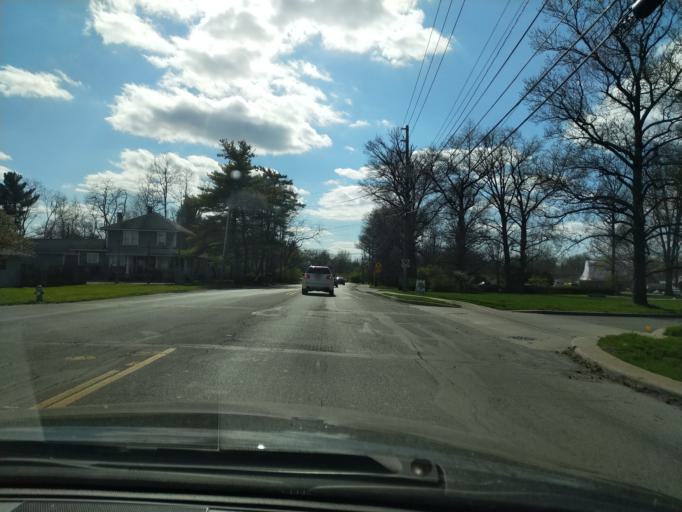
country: US
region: Indiana
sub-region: Marion County
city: Meridian Hills
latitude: 39.8844
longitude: -86.2117
